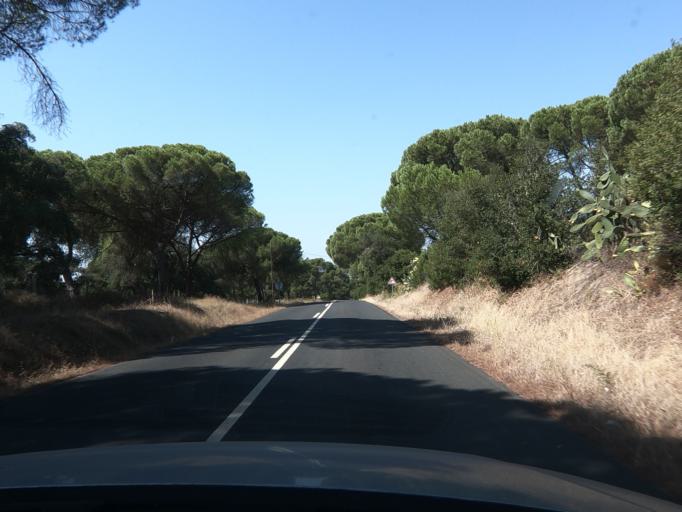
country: PT
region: Setubal
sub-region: Alcacer do Sal
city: Alcacer do Sal
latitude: 38.3512
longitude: -8.4675
